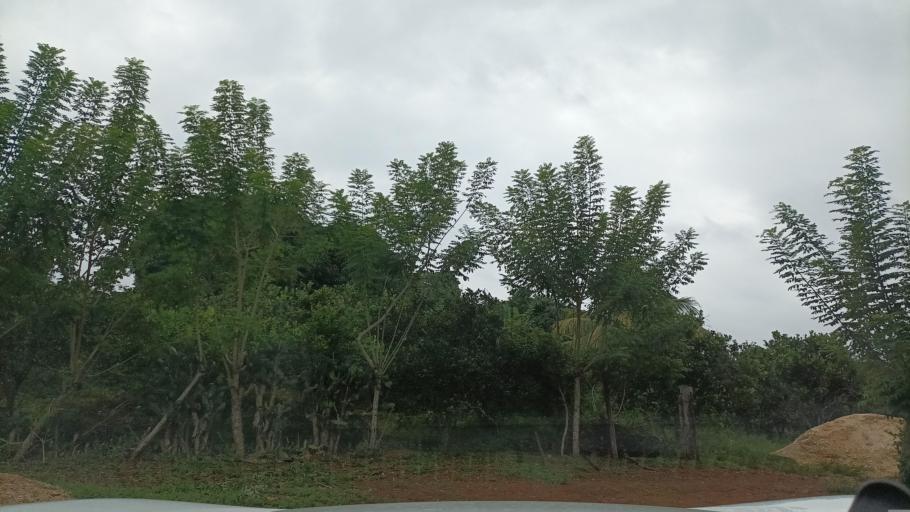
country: MX
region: Veracruz
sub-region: Acayucan
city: Ixhuapan
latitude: 18.0422
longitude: -94.8226
